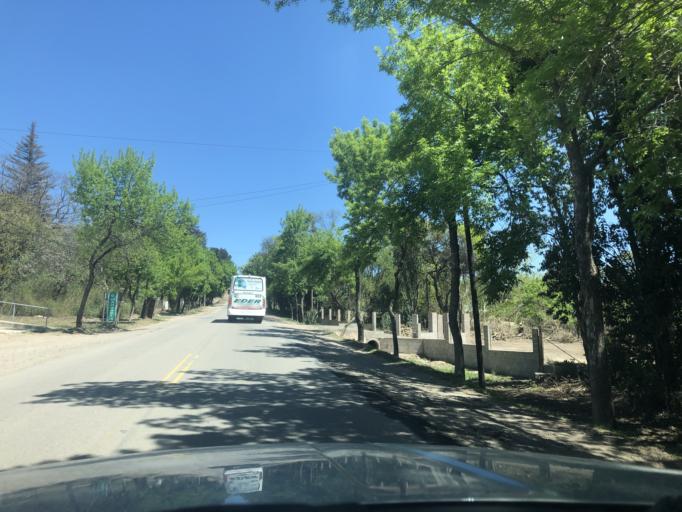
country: AR
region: Cordoba
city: La Granja
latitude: -31.0139
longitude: -64.2707
